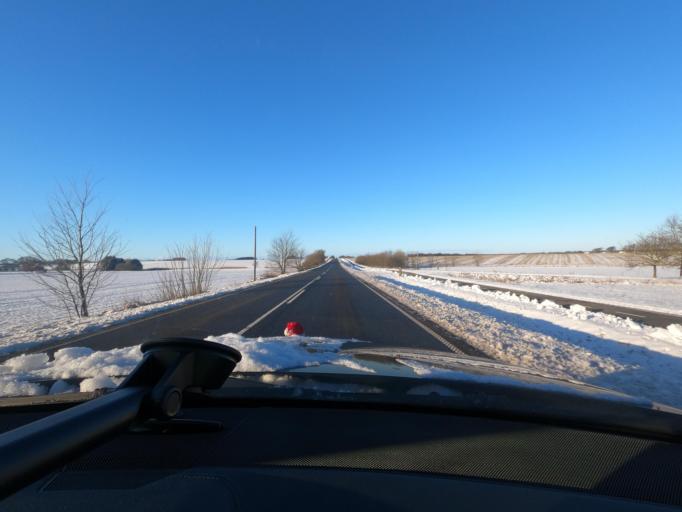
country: DK
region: South Denmark
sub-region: Tonder Kommune
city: Toftlund
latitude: 55.1482
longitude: 9.1100
